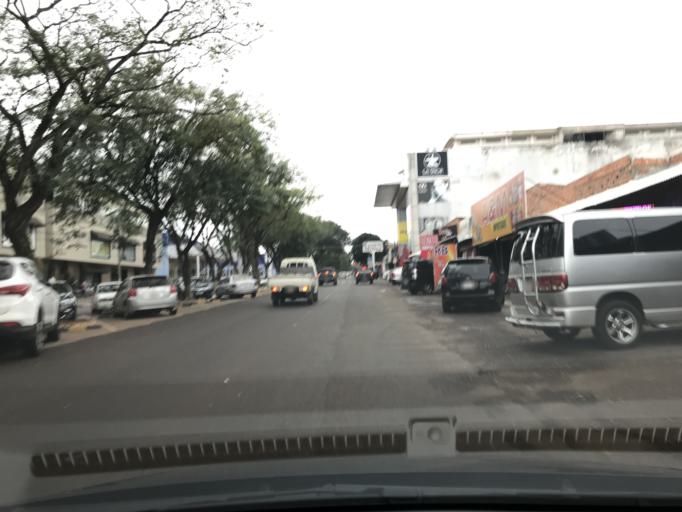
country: PY
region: Canindeyu
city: Salto del Guaira
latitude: -24.0583
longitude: -54.3068
